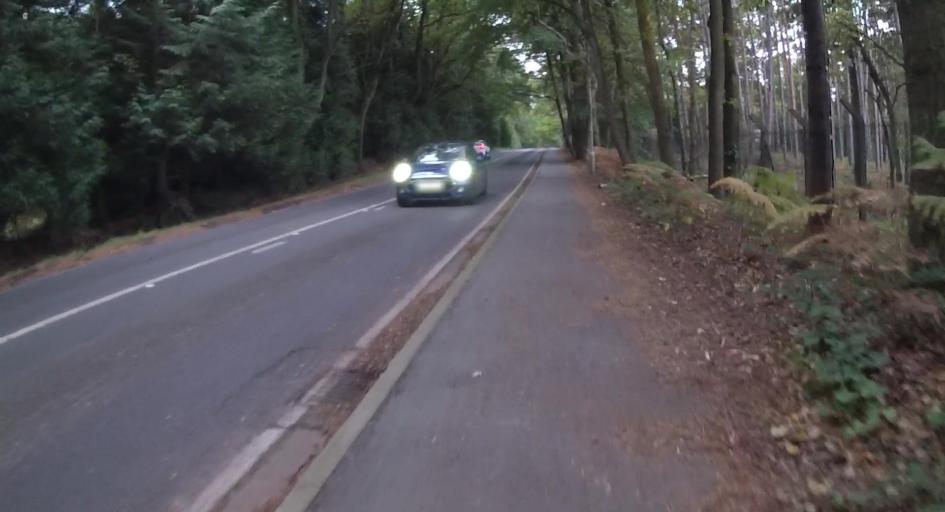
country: GB
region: England
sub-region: Bracknell Forest
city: Crowthorne
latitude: 51.3792
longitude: -0.7794
